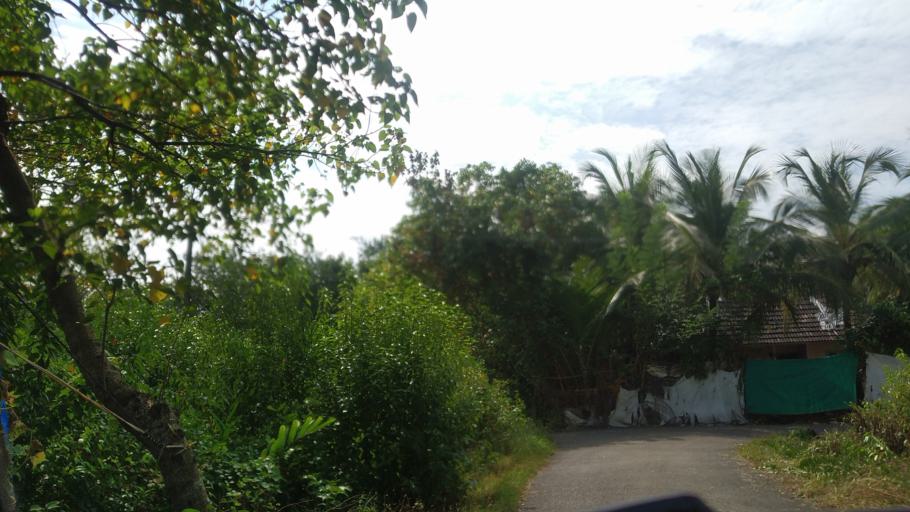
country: IN
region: Kerala
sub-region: Ernakulam
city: Elur
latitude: 10.0818
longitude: 76.2022
